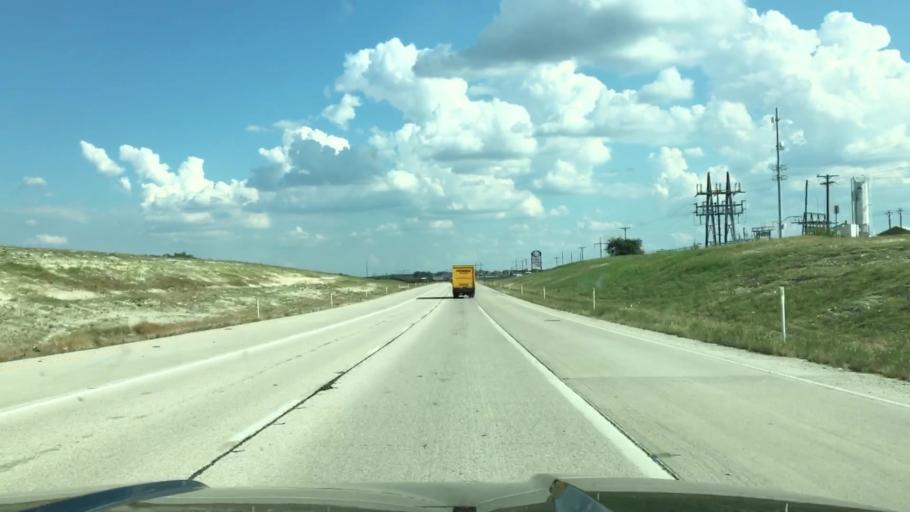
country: US
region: Texas
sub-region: Wise County
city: Decatur
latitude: 33.1795
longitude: -97.5473
